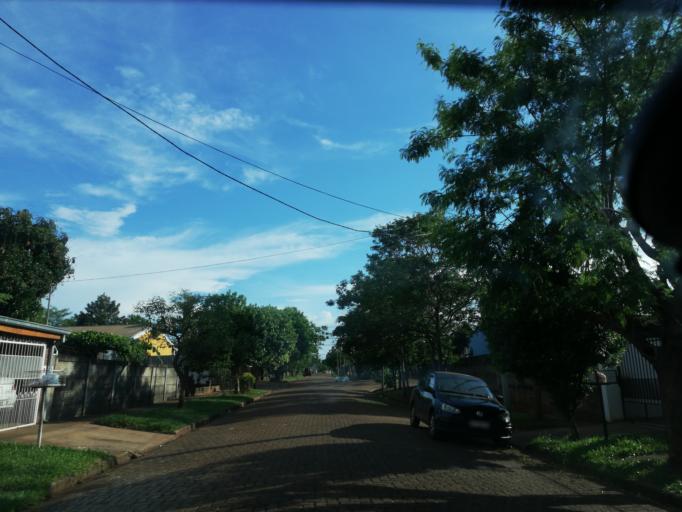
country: AR
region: Misiones
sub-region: Departamento de Capital
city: Posadas
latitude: -27.4051
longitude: -55.9547
